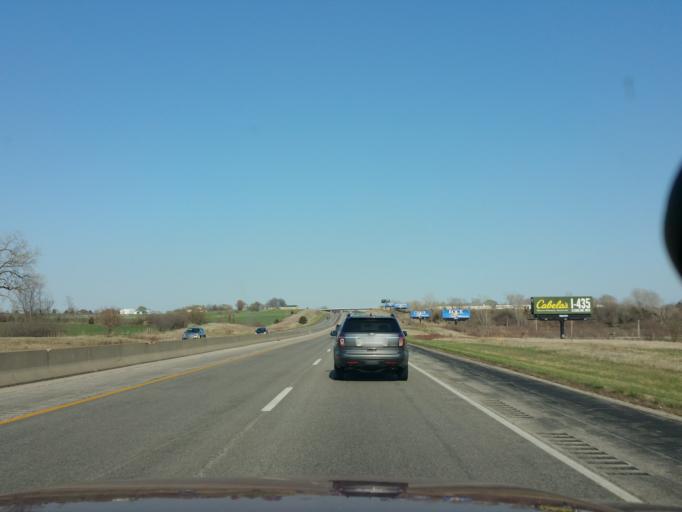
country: US
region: Kansas
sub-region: Leavenworth County
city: Basehor
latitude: 39.0808
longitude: -94.9582
